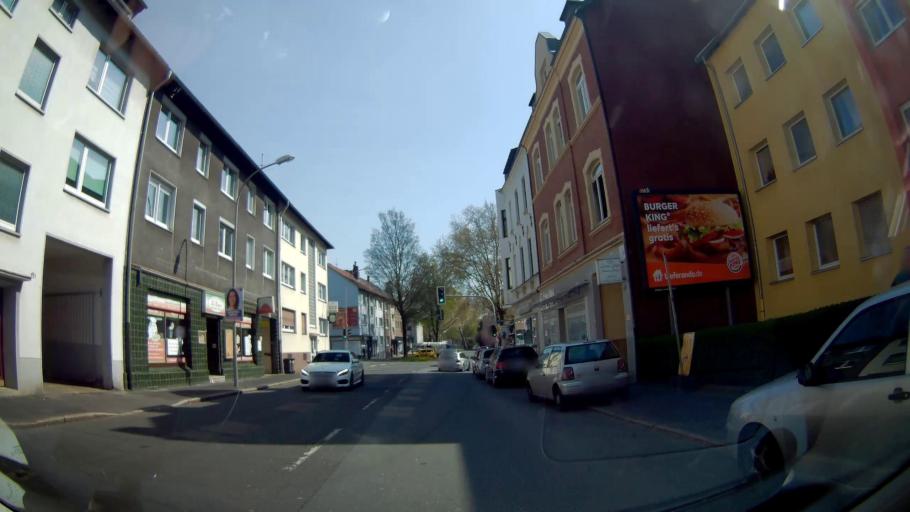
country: DE
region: North Rhine-Westphalia
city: Bochum-Hordel
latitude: 51.4924
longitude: 7.1910
